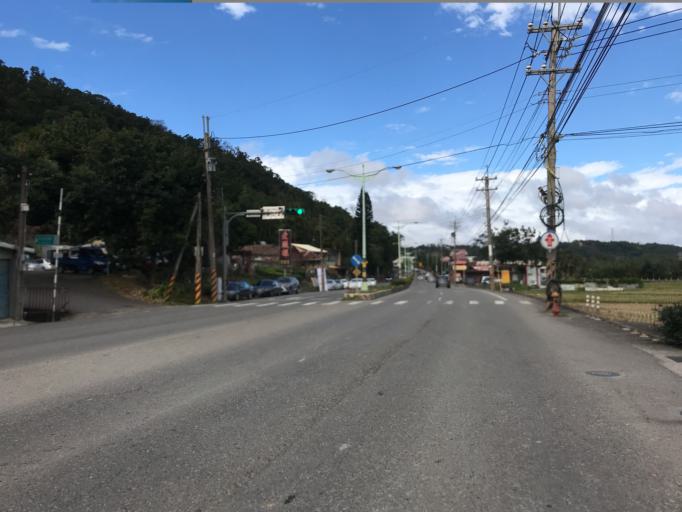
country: TW
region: Taiwan
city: Daxi
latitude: 24.8353
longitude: 121.2460
